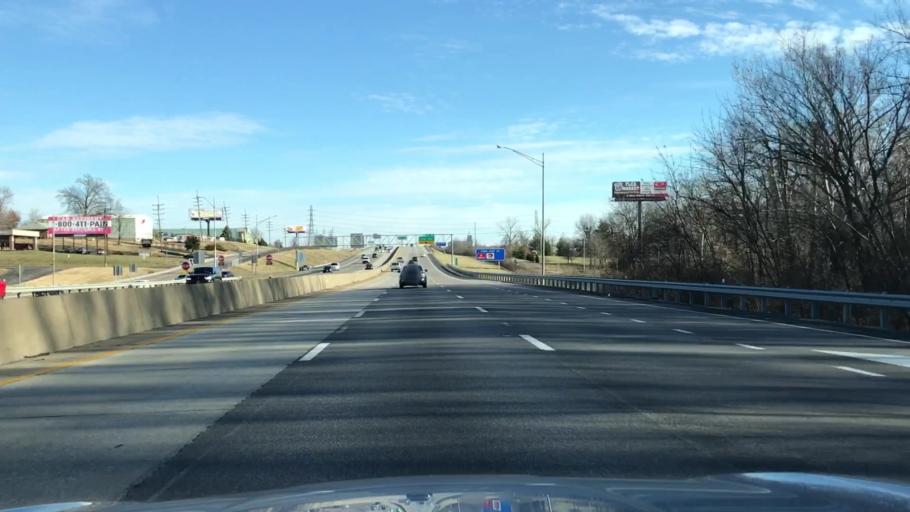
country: US
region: Missouri
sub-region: Saint Louis County
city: Spanish Lake
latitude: 38.7691
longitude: -90.2167
